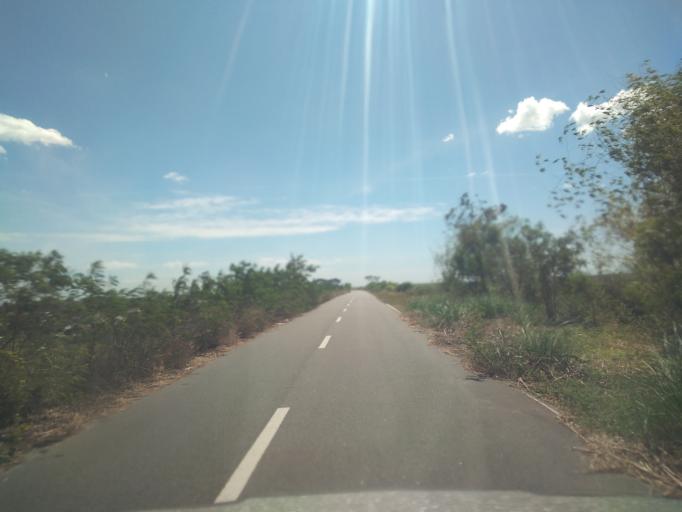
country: PH
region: Central Luzon
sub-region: Province of Pampanga
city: San Basilio
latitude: 15.0250
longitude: 120.6002
